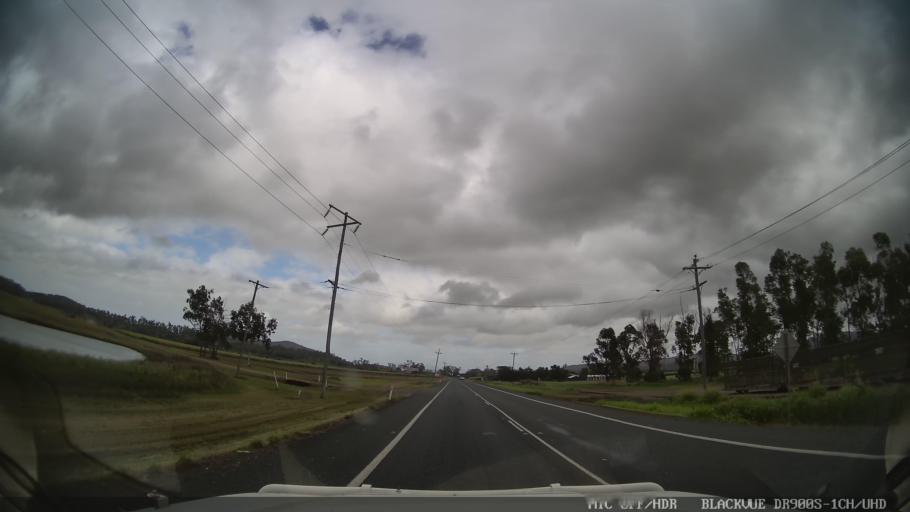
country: AU
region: Queensland
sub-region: Whitsunday
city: Proserpine
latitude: -20.3444
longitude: 148.6306
